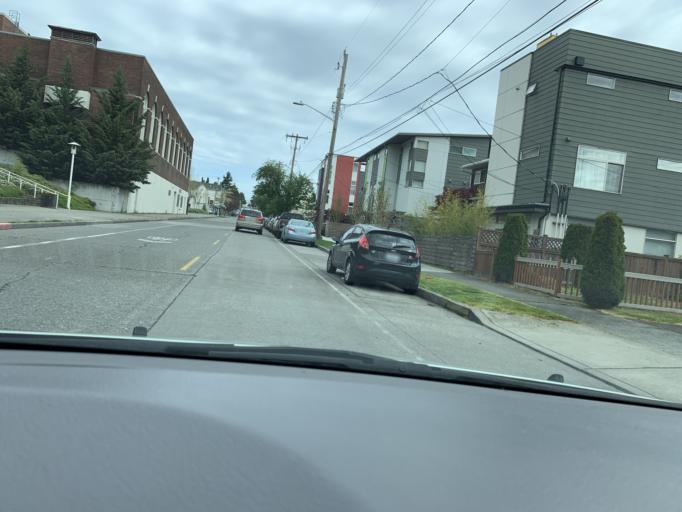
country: US
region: Washington
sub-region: King County
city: White Center
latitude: 47.5517
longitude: -122.3135
